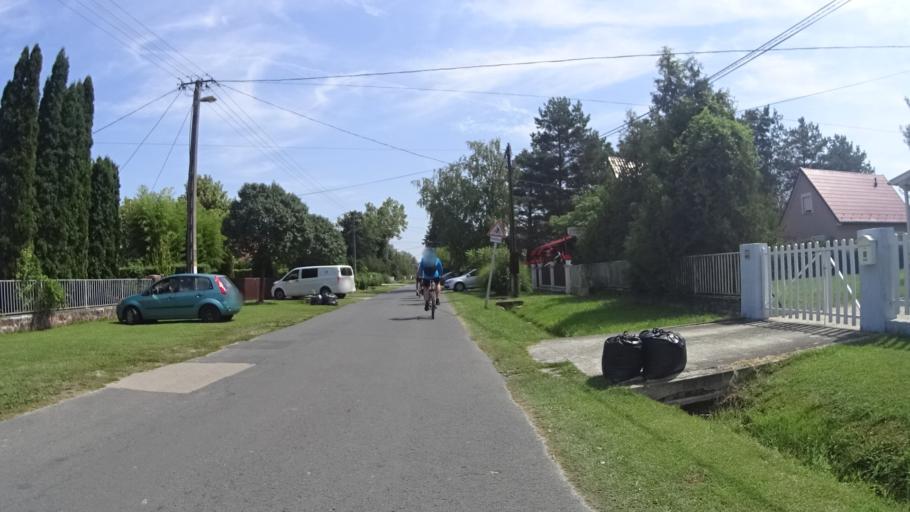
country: HU
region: Somogy
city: Kethely
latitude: 46.7045
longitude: 17.4218
